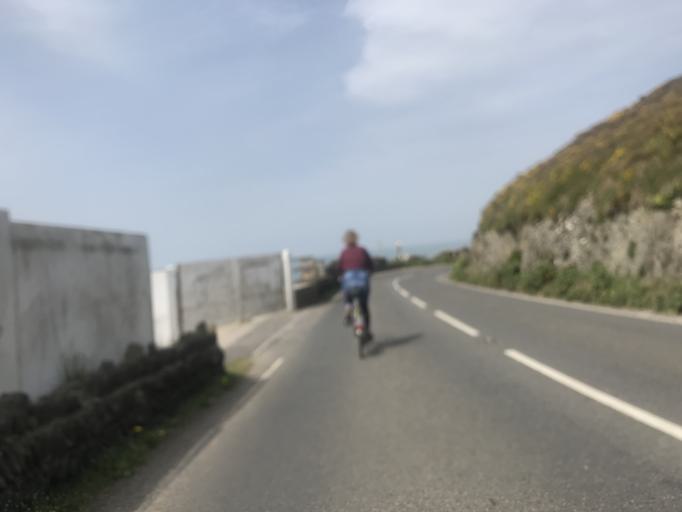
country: GB
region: England
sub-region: Devon
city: Braunton
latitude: 51.1224
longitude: -4.2398
